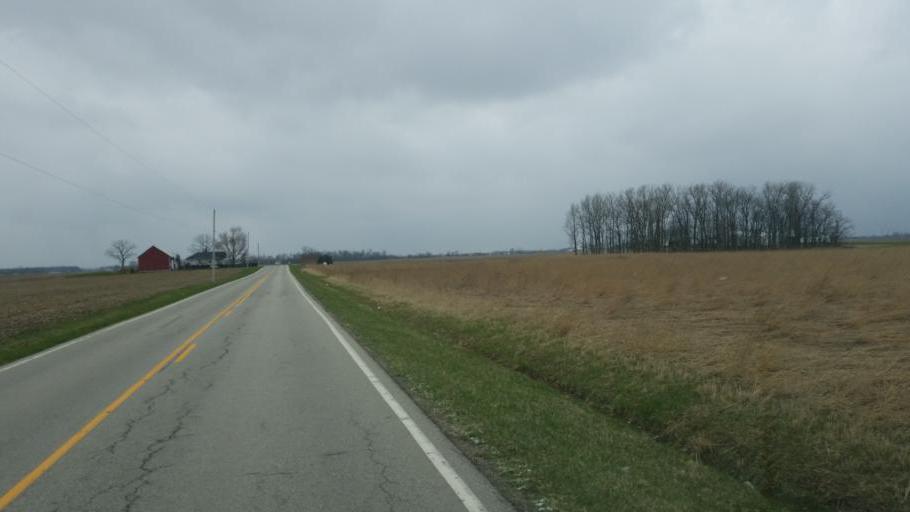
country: US
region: Ohio
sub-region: Union County
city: Richwood
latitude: 40.4366
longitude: -83.3888
